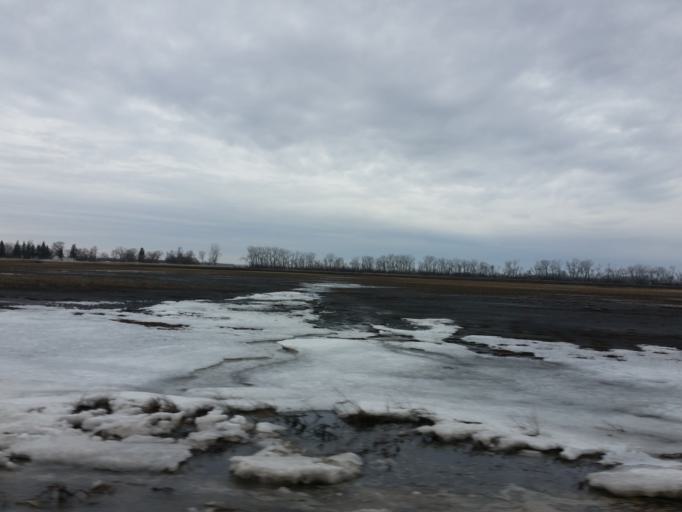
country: US
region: North Dakota
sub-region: Walsh County
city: Grafton
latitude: 48.3997
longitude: -97.4703
